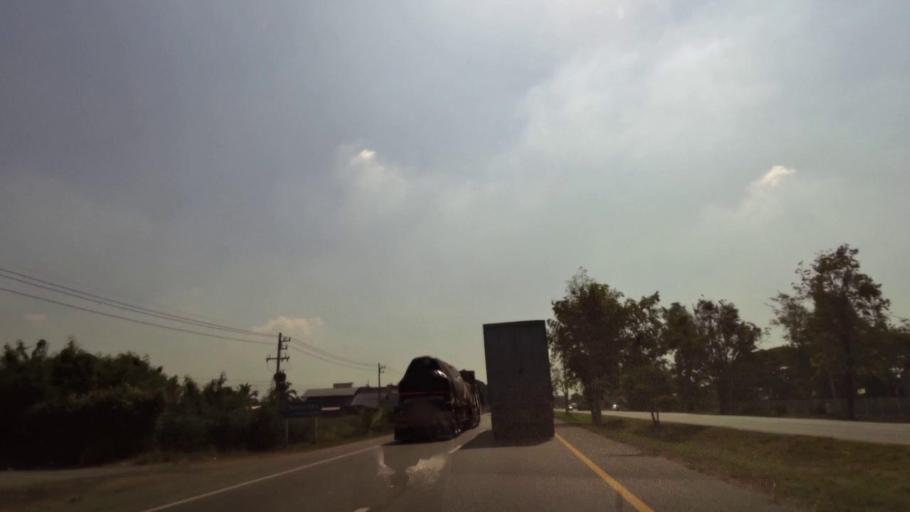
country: TH
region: Phichit
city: Bueng Na Rang
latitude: 16.1361
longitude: 100.1255
